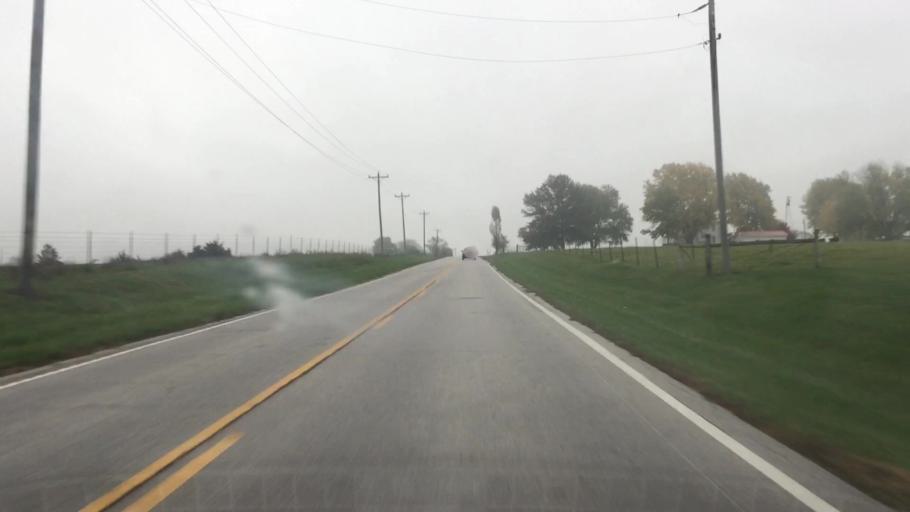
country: US
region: Missouri
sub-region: Callaway County
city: Fulton
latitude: 38.8739
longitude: -92.0628
